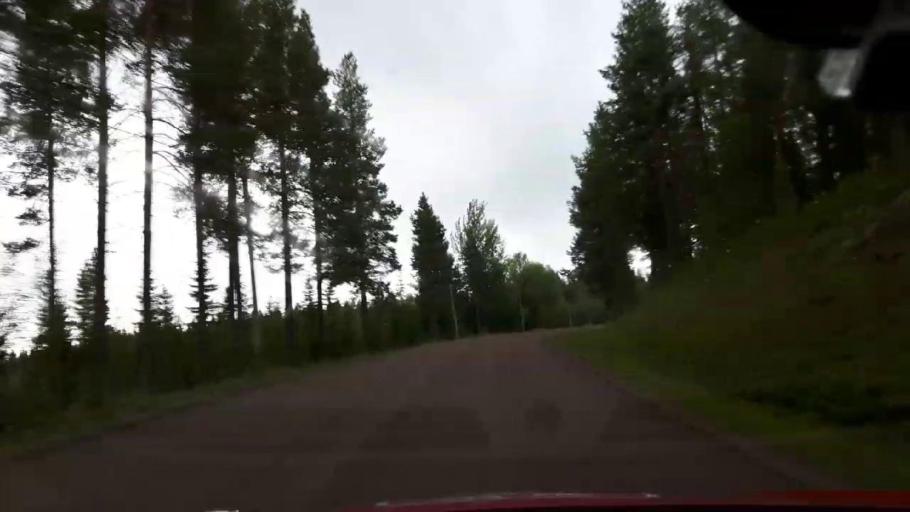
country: SE
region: Jaemtland
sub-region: Are Kommun
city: Jarpen
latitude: 63.3174
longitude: 13.6942
